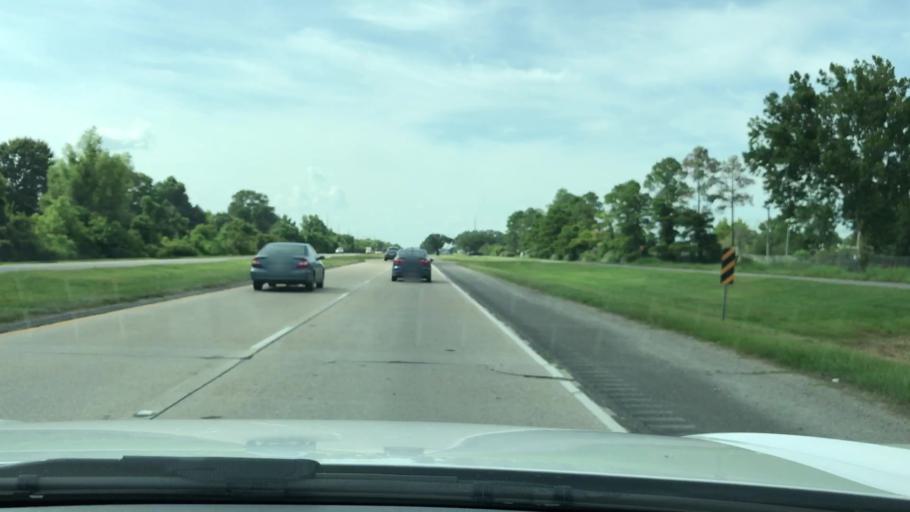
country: US
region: Louisiana
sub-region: Iberville Parish
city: Plaquemine
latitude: 30.3174
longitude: -91.2502
